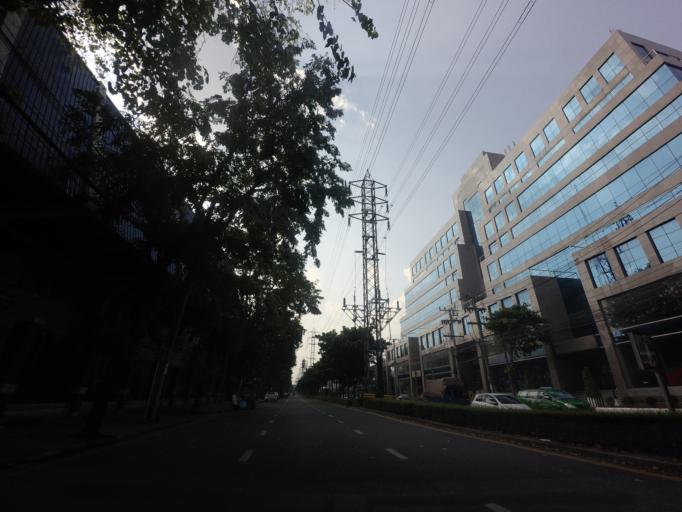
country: TH
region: Bangkok
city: Pathum Wan
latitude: 13.7340
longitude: 100.5456
